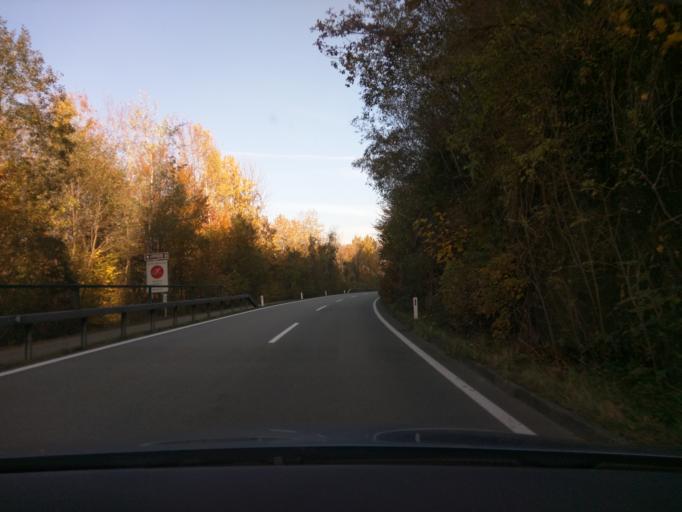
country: DE
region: Bavaria
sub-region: Lower Bavaria
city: Salzweg
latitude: 48.5841
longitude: 13.5059
